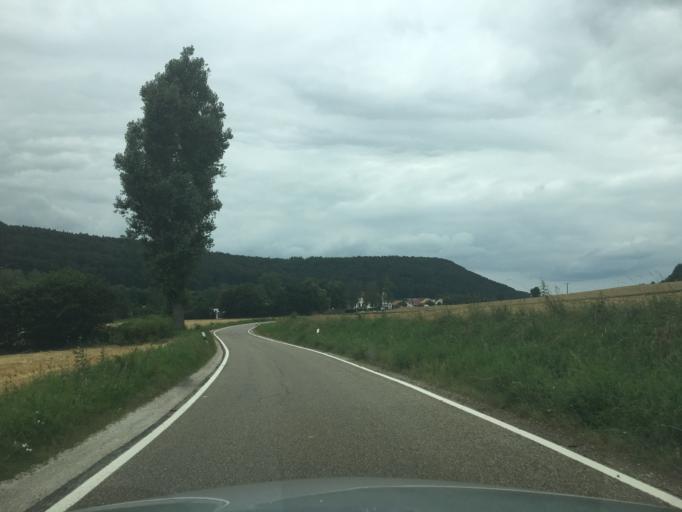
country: DE
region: Bavaria
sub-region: Regierungsbezirk Mittelfranken
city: Greding
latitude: 49.0272
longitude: 11.3740
